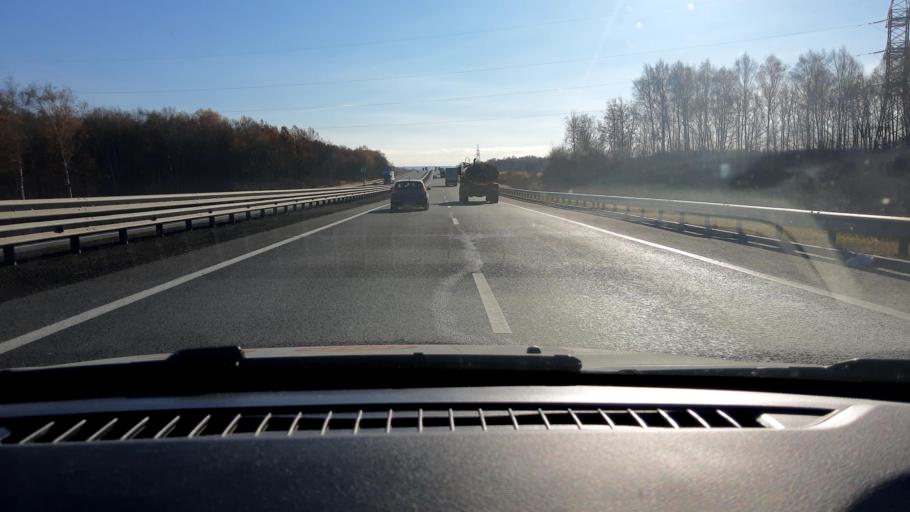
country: RU
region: Nizjnij Novgorod
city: Burevestnik
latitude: 56.1407
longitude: 43.7616
